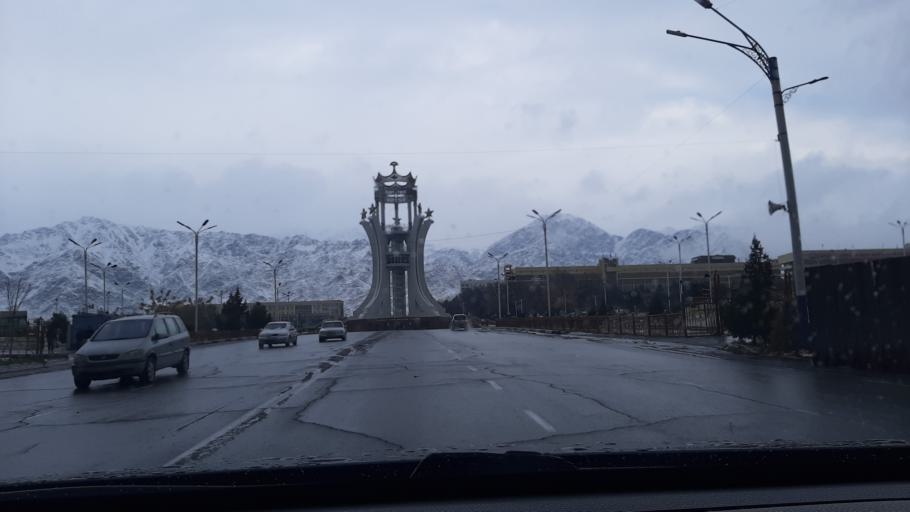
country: TJ
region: Viloyati Sughd
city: Khujand
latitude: 40.3001
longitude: 69.6146
